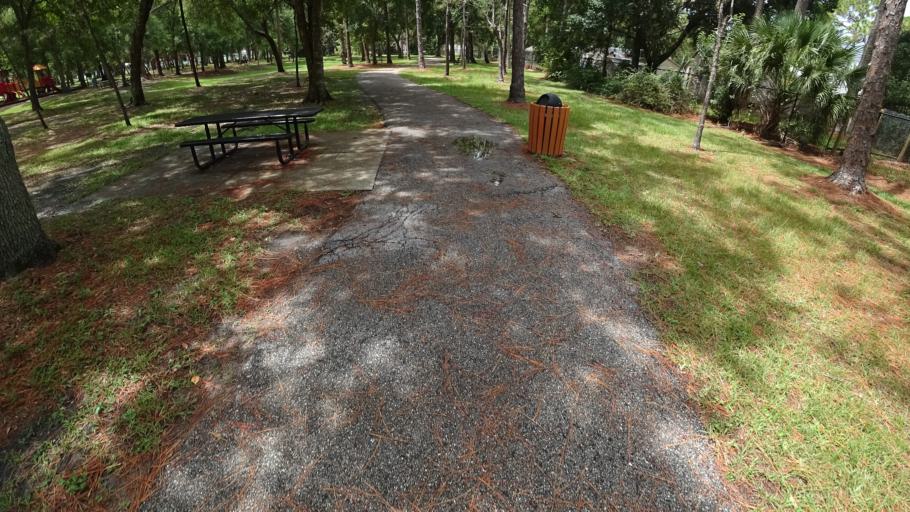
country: US
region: Florida
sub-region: Manatee County
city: Whitfield
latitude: 27.4321
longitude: -82.5568
